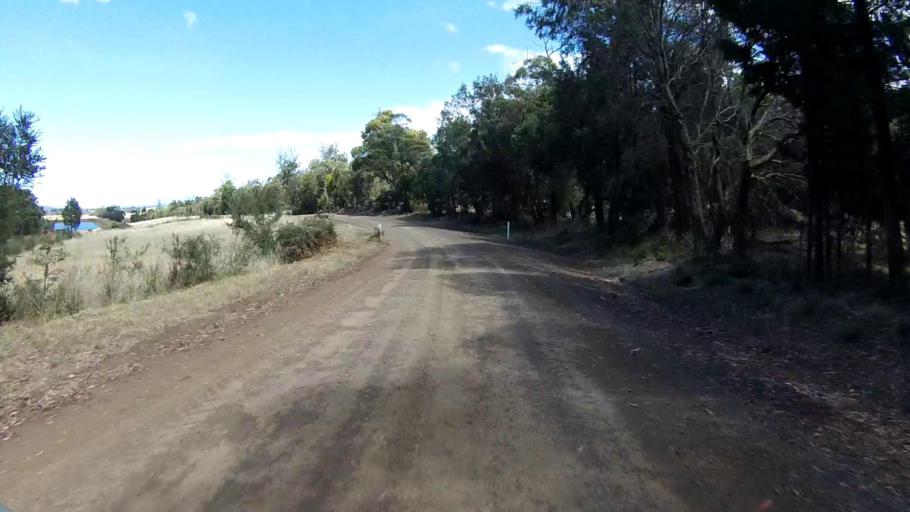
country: AU
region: Tasmania
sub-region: Break O'Day
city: St Helens
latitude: -41.9832
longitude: 148.0654
